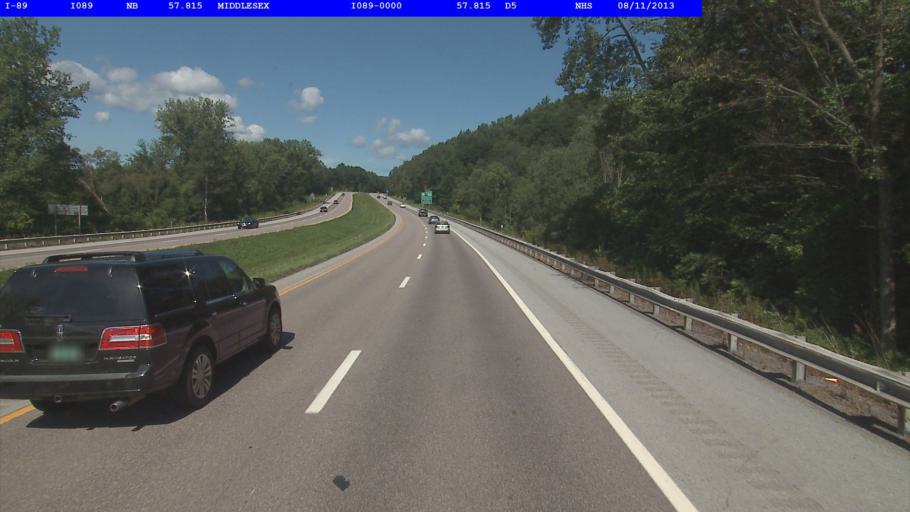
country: US
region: Vermont
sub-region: Washington County
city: Waterbury
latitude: 44.2917
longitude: -72.6696
